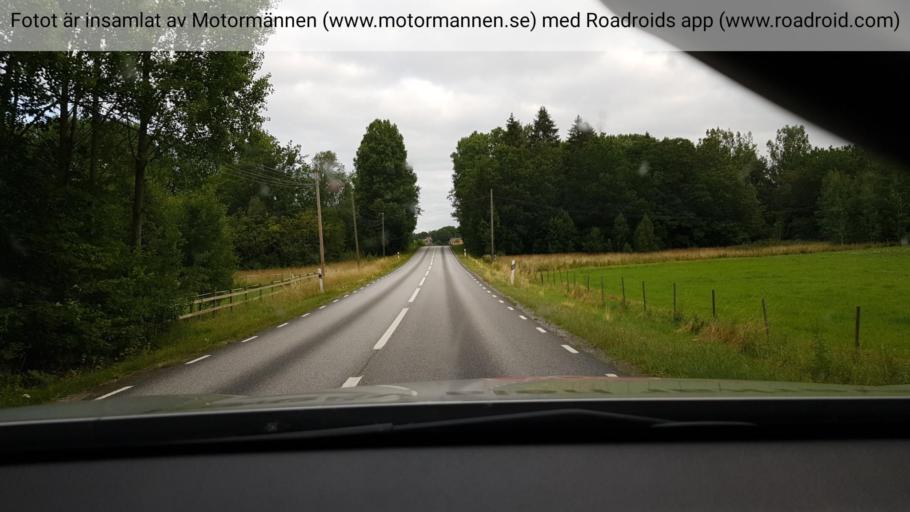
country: SE
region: Stockholm
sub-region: Norrtalje Kommun
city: Skanninge
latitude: 59.8355
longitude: 18.4420
